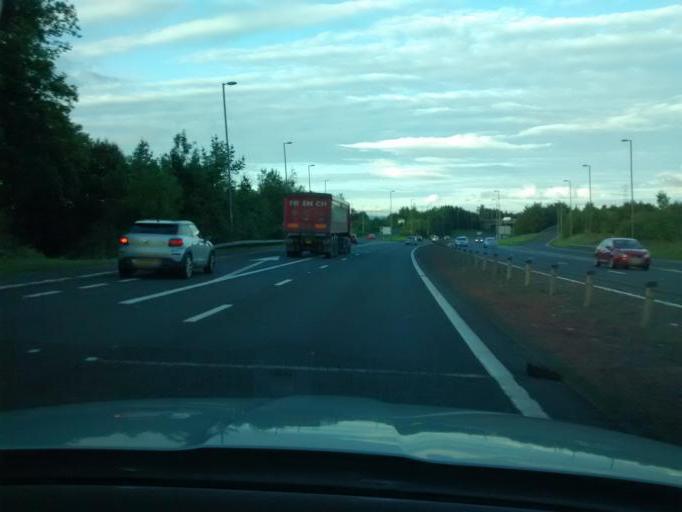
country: GB
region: Scotland
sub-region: Renfrewshire
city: Johnstone
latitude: 55.8375
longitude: -4.5244
